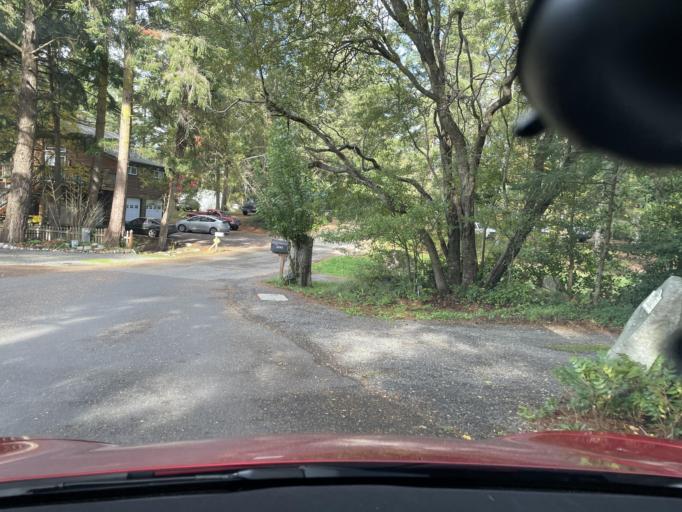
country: US
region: Washington
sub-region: San Juan County
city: Friday Harbor
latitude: 48.5334
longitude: -123.0293
